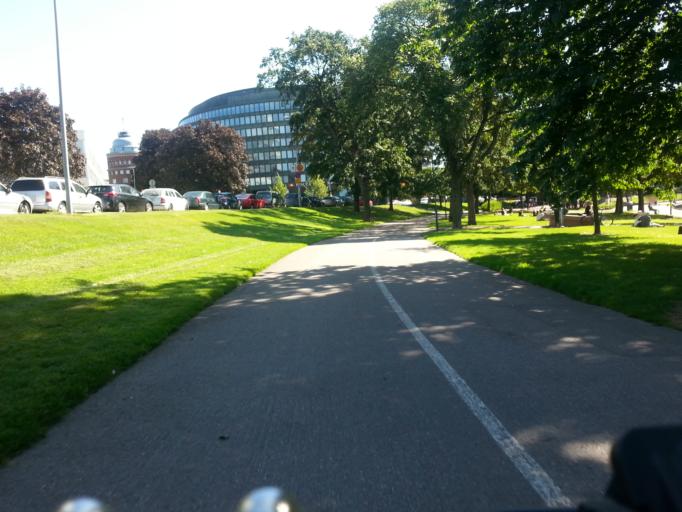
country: FI
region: Uusimaa
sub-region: Helsinki
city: Helsinki
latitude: 60.1808
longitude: 24.9458
